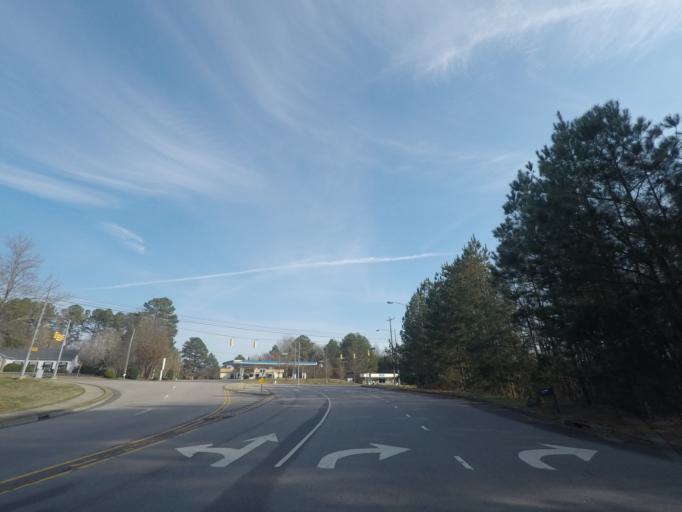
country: US
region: North Carolina
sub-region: Durham County
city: Durham
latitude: 36.0831
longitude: -78.9324
